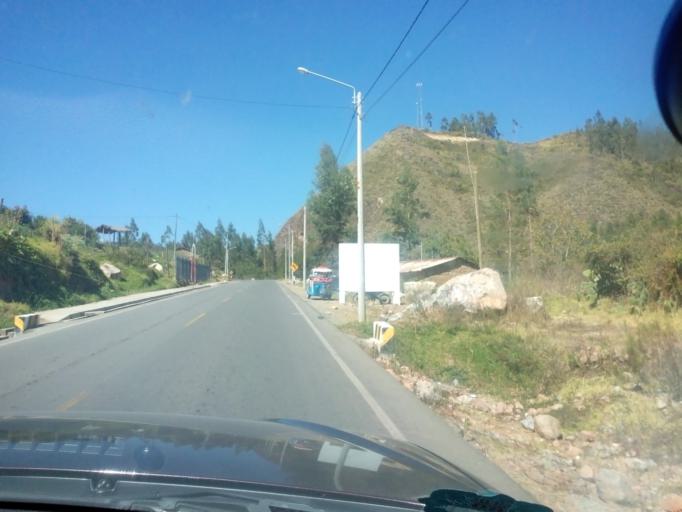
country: PE
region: Apurimac
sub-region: Chincheros
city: Chincheros
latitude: -13.5148
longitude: -73.7095
